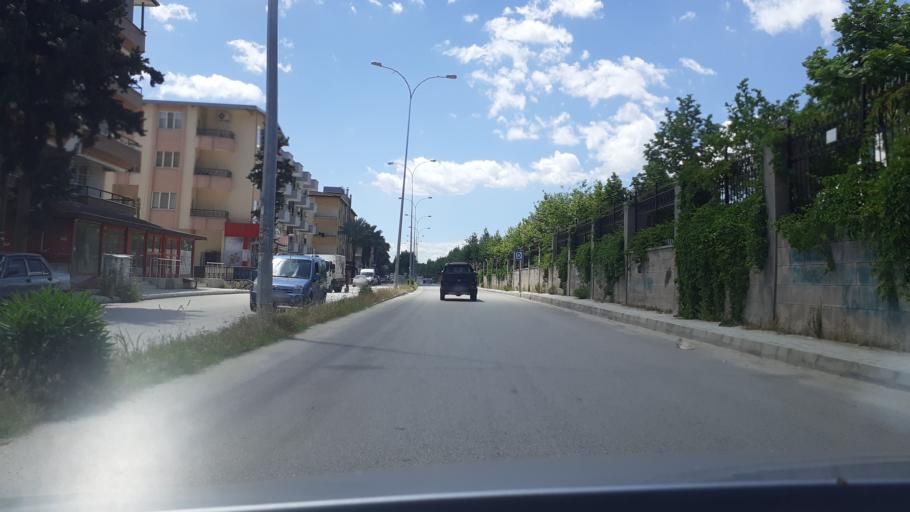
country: TR
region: Hatay
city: Anayazi
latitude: 36.3365
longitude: 36.2001
